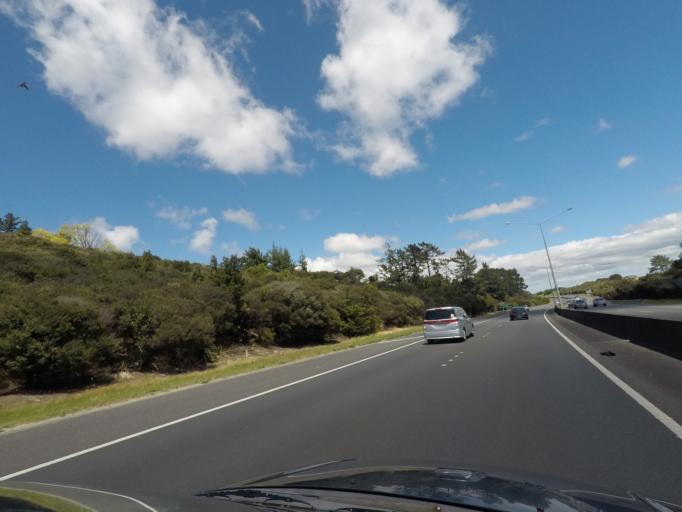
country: NZ
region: Auckland
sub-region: Auckland
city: Rothesay Bay
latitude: -36.7640
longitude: 174.6961
